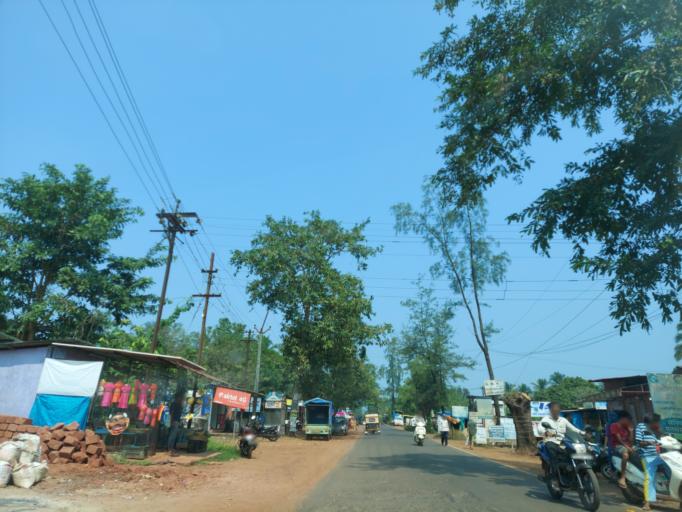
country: IN
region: Maharashtra
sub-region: Sindhudurg
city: Kudal
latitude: 15.9891
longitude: 73.6833
